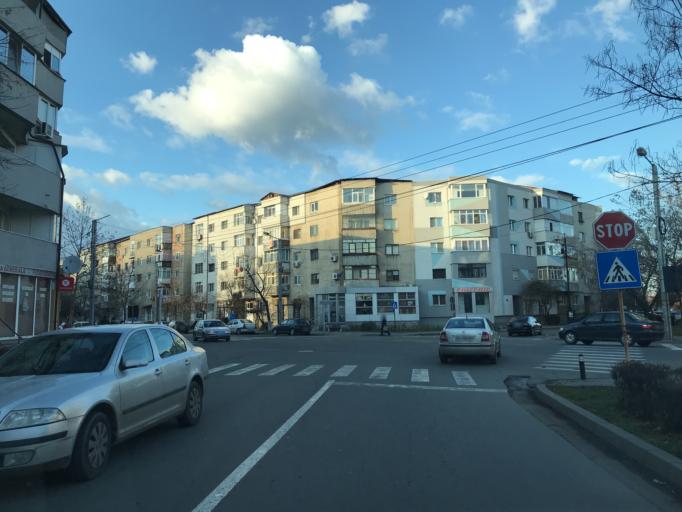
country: RO
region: Olt
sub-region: Municipiul Slatina
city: Slatina
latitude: 44.4230
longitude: 24.3815
